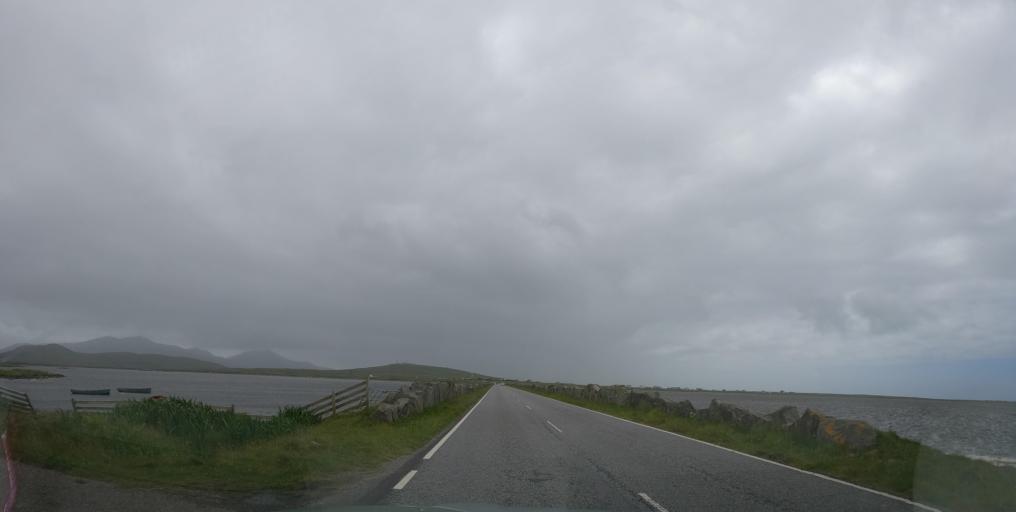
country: GB
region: Scotland
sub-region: Eilean Siar
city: Benbecula
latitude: 57.3628
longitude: -7.3546
